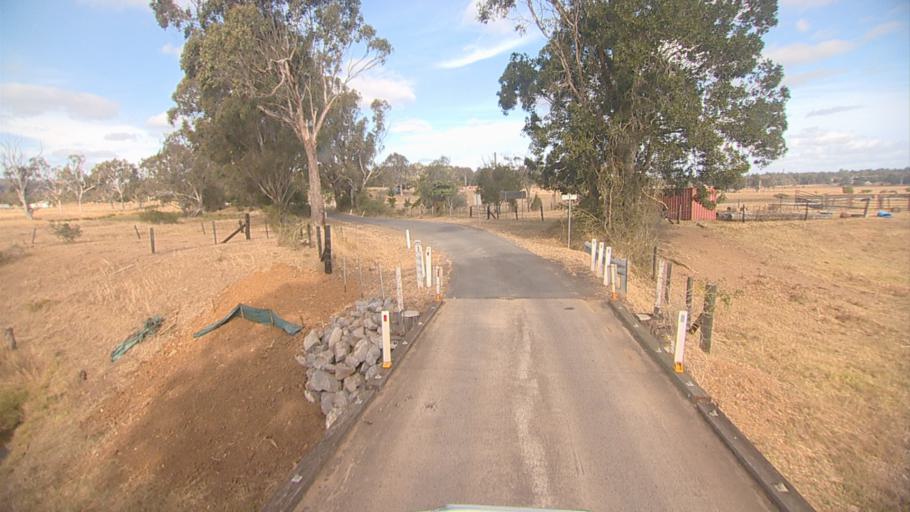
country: AU
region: Queensland
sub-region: Logan
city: Cedar Vale
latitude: -27.9173
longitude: 153.0003
